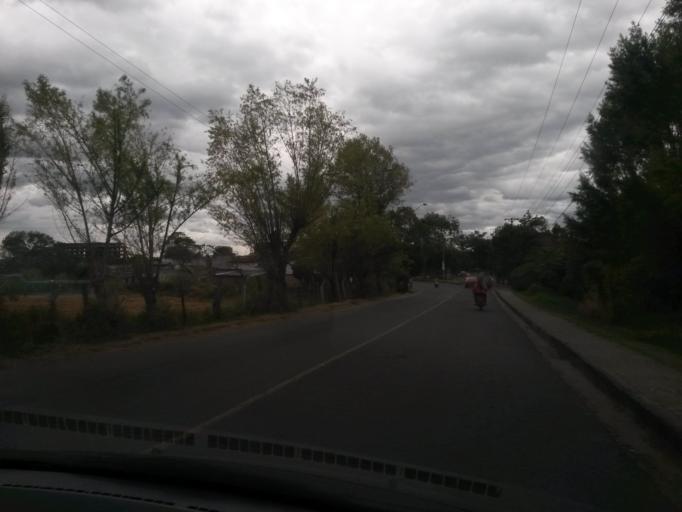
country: CO
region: Cauca
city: Popayan
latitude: 2.4587
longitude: -76.5984
